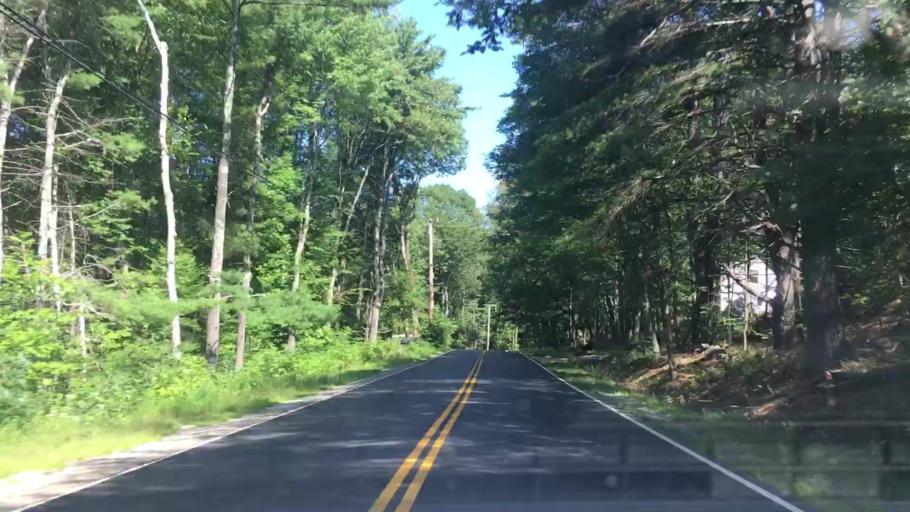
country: US
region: Maine
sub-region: Sagadahoc County
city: Topsham
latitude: 43.9841
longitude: -69.9859
